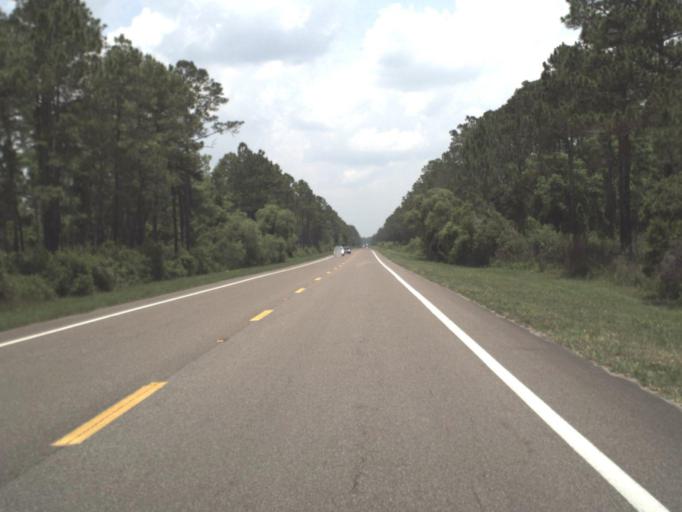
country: US
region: Florida
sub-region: Putnam County
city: Palatka
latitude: 29.4452
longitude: -81.7379
